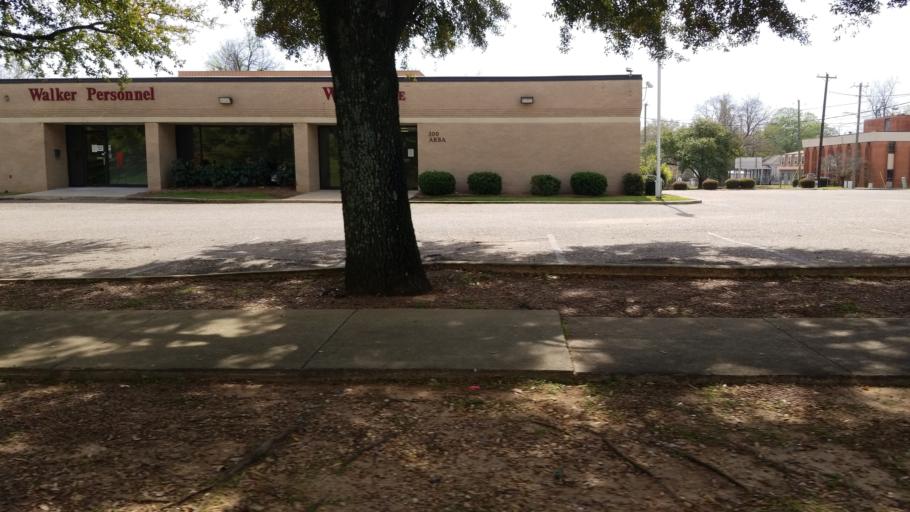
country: US
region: Alabama
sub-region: Montgomery County
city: Montgomery
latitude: 32.3673
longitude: -86.3043
